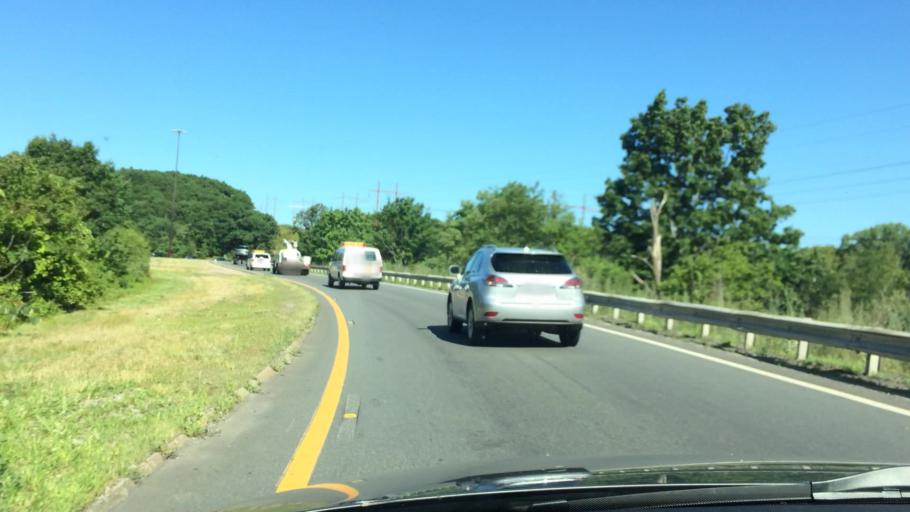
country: US
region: Massachusetts
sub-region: Middlesex County
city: Lexington
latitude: 42.4785
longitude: -71.2189
